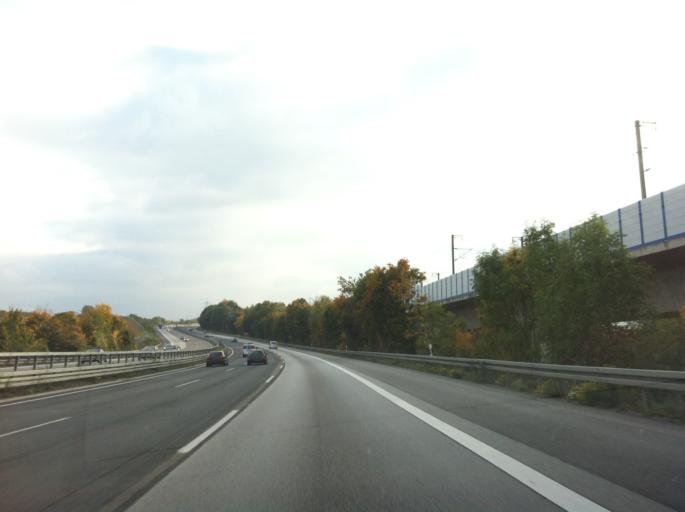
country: DE
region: Hesse
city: Bad Camberg
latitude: 50.2585
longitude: 8.2480
